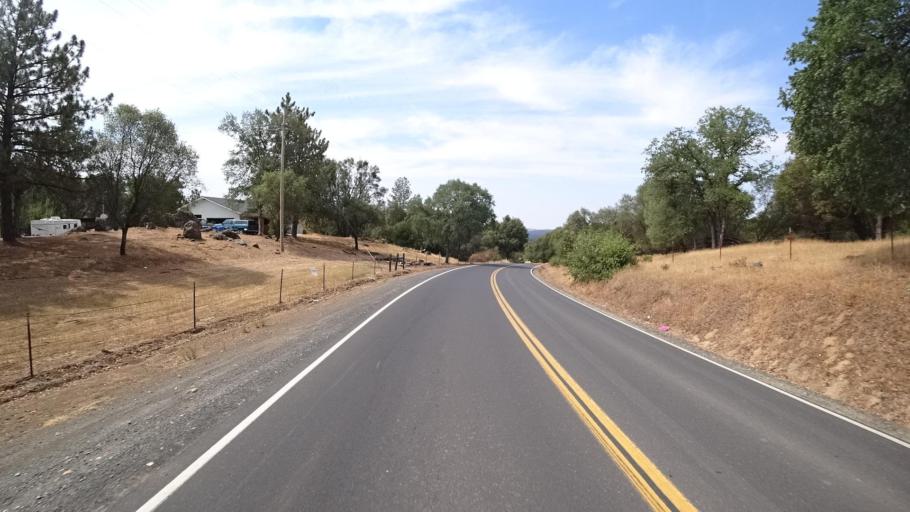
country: US
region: California
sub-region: Mariposa County
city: Midpines
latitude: 37.4784
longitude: -119.8691
